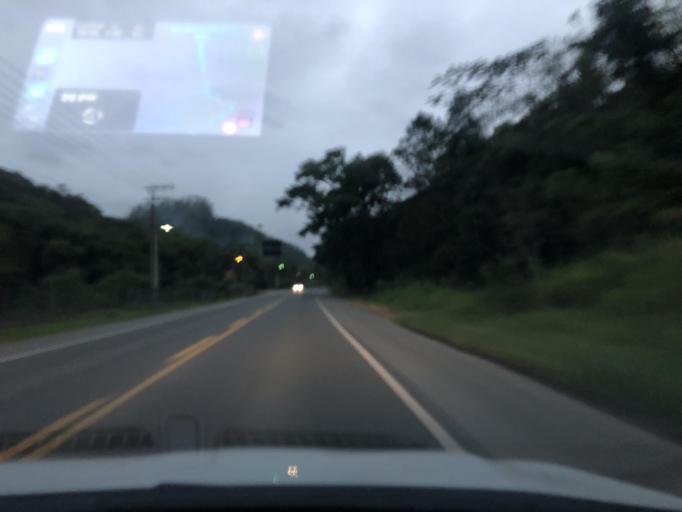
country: BR
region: Santa Catarina
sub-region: Pomerode
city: Pomerode
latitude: -26.6666
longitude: -49.0343
